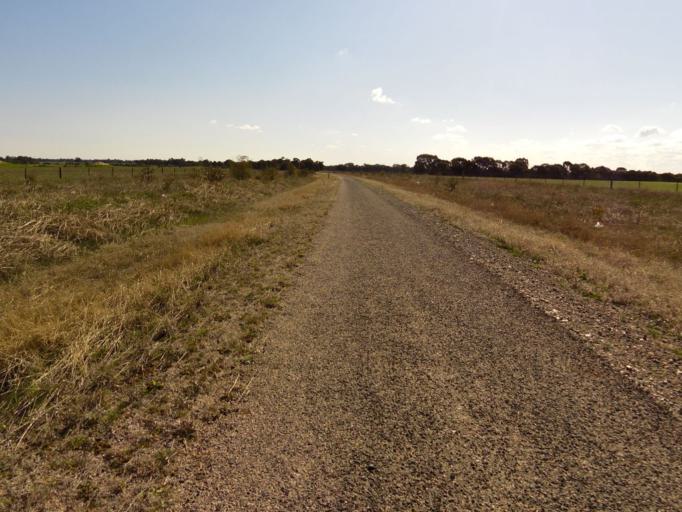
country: AU
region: New South Wales
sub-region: Corowa Shire
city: Corowa
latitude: -36.0354
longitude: 146.4493
